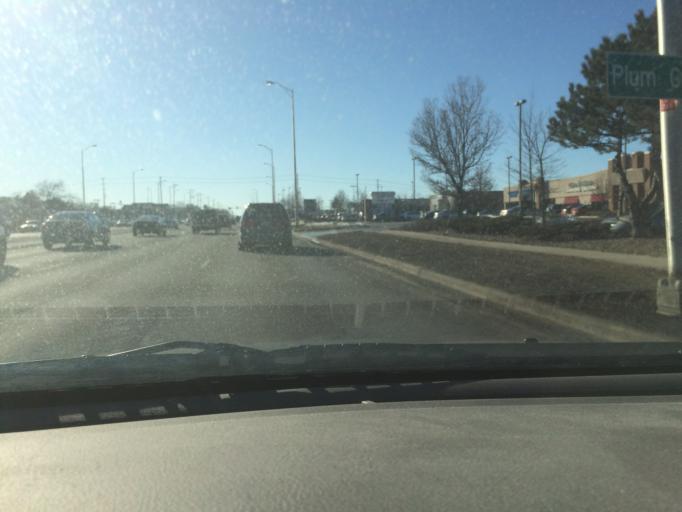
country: US
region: Illinois
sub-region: Cook County
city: Hoffman Estates
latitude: 42.0502
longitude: -88.0566
